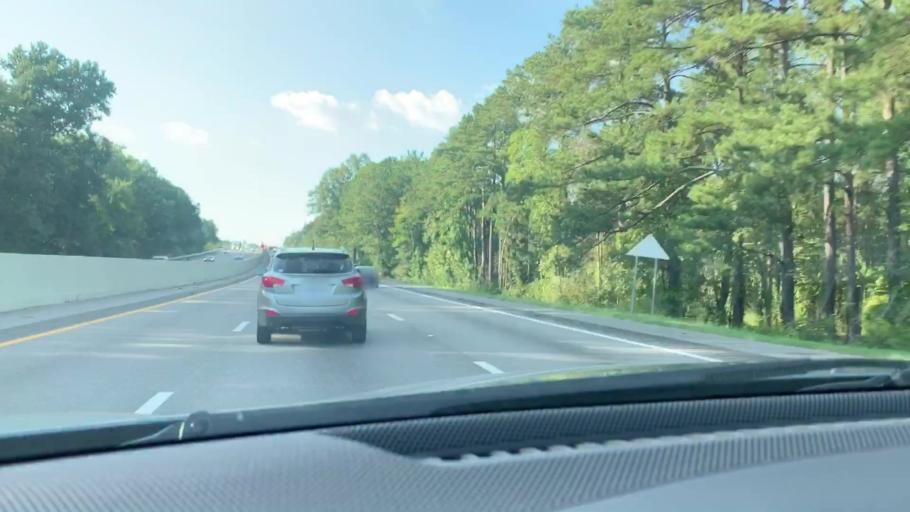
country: US
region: South Carolina
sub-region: Lexington County
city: Pineridge
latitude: 33.9130
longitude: -81.0579
